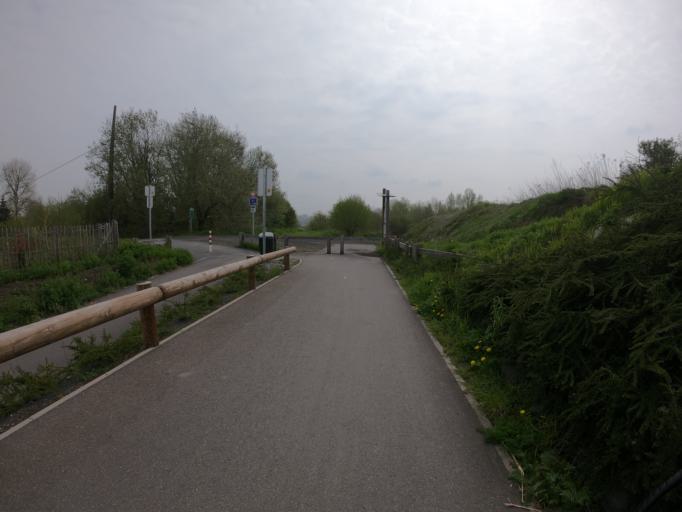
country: BE
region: Flanders
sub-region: Provincie West-Vlaanderen
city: Avelgem
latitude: 50.7609
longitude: 3.4563
